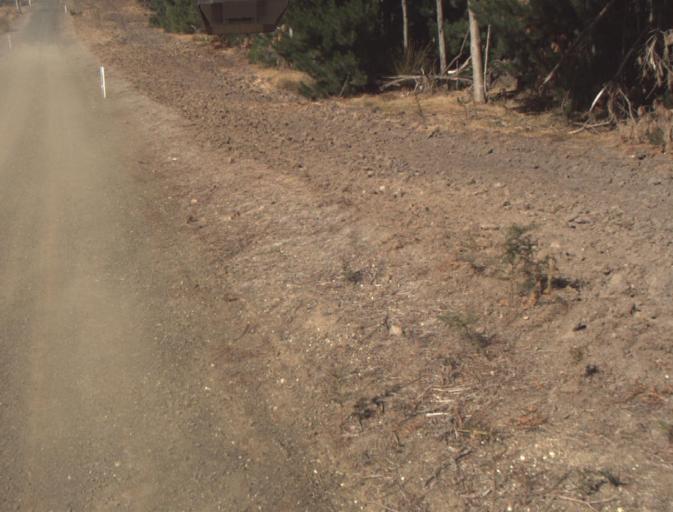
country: AU
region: Tasmania
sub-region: Dorset
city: Bridport
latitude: -41.1596
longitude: 147.2120
